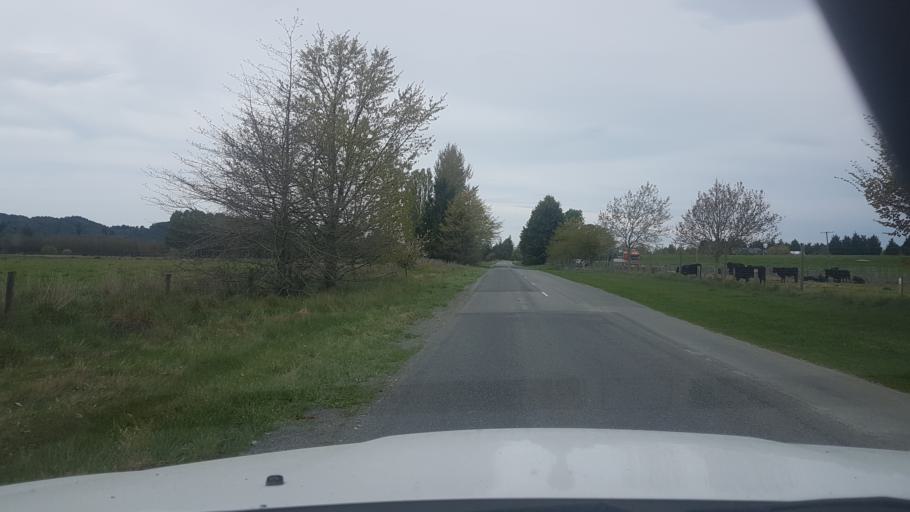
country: NZ
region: Canterbury
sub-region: Timaru District
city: Pleasant Point
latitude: -44.0782
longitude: 171.1757
